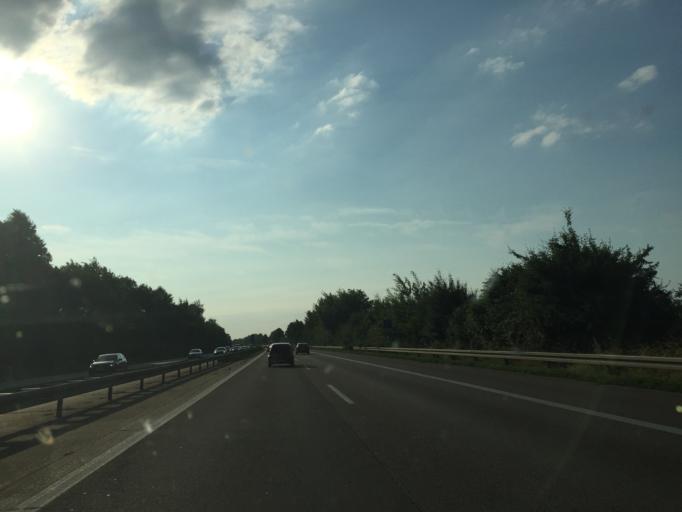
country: DE
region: Baden-Wuerttemberg
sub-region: Regierungsbezirk Stuttgart
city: Leingarten
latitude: 49.1909
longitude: 9.1141
